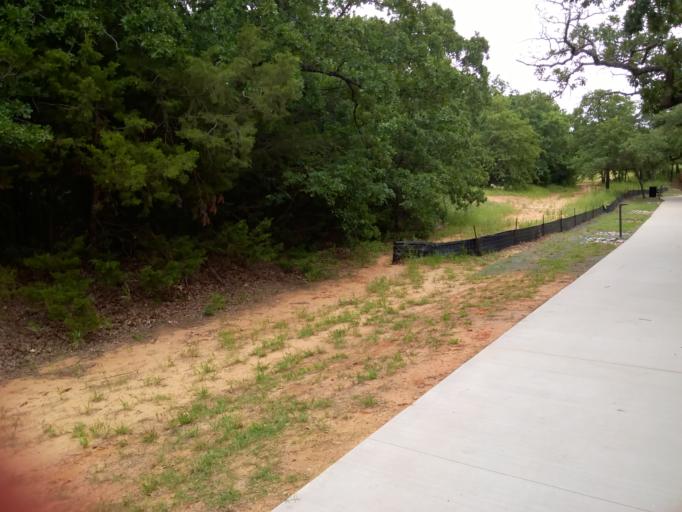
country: US
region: Texas
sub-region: Denton County
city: Flower Mound
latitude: 32.9875
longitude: -97.0687
